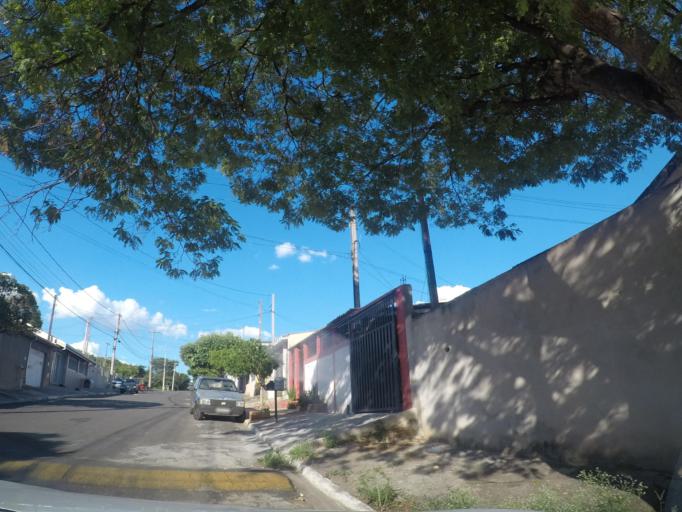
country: BR
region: Sao Paulo
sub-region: Sumare
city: Sumare
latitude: -22.8114
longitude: -47.2252
